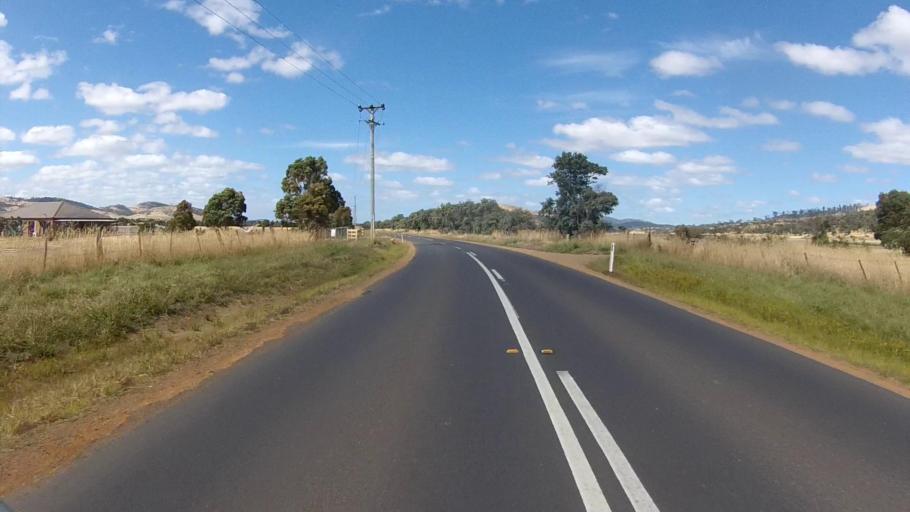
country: AU
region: Tasmania
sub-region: Clarence
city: Cambridge
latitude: -42.7113
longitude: 147.4300
